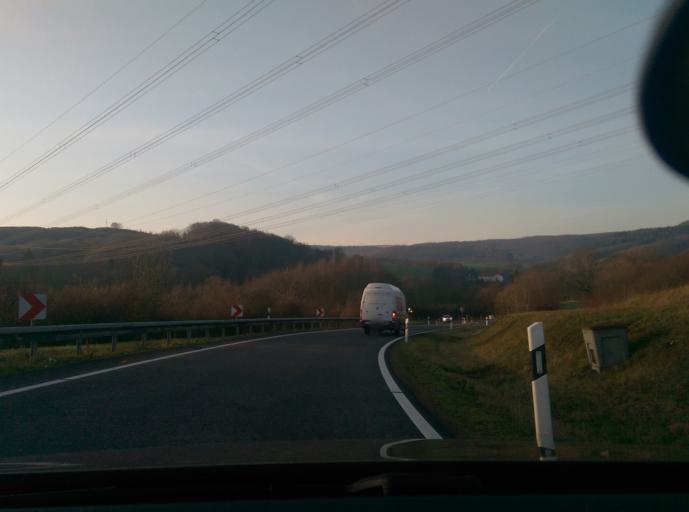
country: DE
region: Thuringia
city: Lauchroden
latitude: 51.0176
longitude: 10.1207
